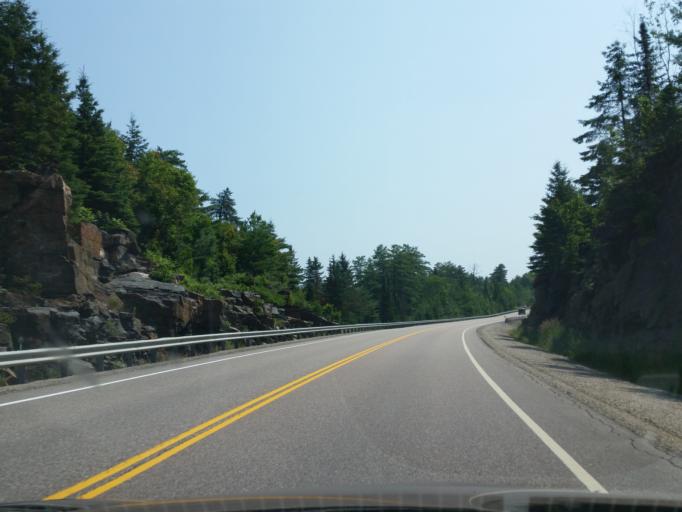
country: CA
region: Ontario
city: Deep River
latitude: 46.1834
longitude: -77.7522
